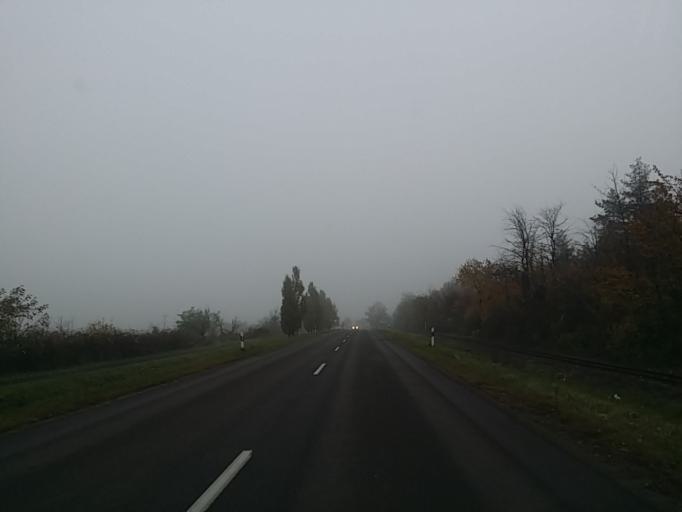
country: HU
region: Heves
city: Gyongyossolymos
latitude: 47.8139
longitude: 19.9583
